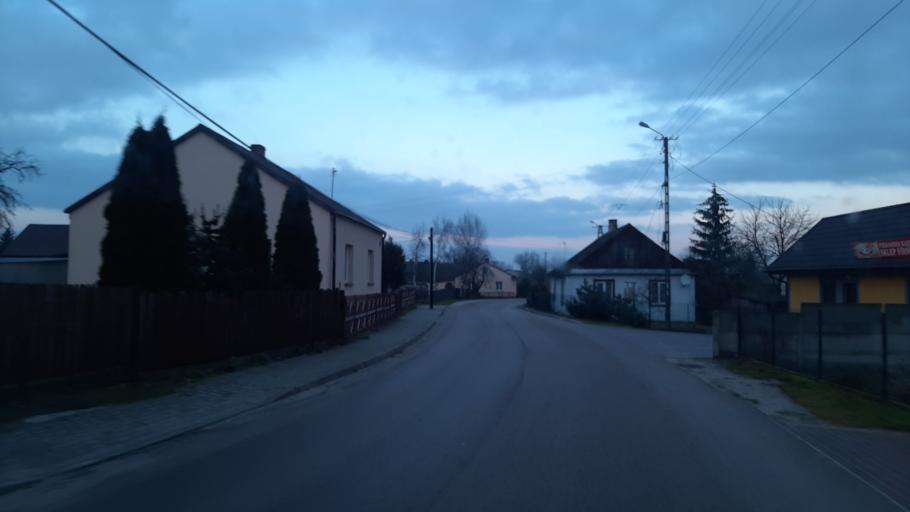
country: PL
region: Lublin Voivodeship
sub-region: Powiat lubartowski
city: Firlej
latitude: 51.5698
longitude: 22.5344
